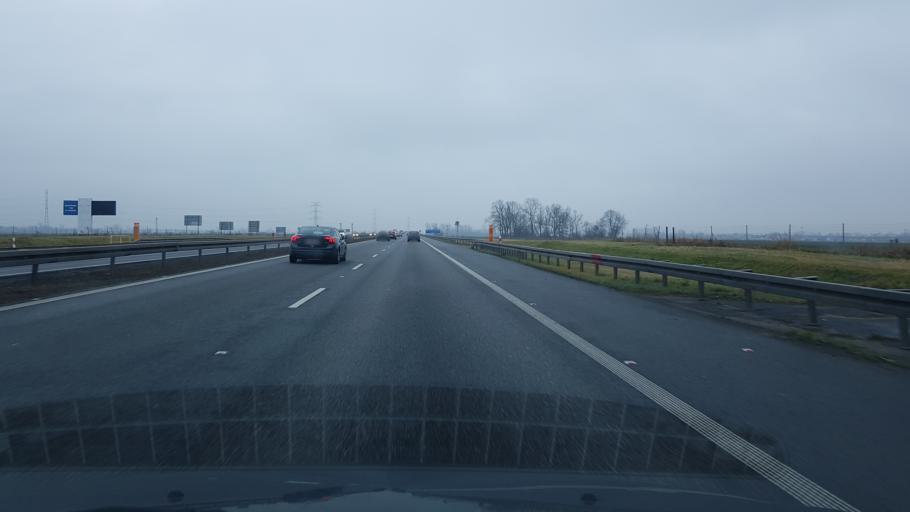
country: PL
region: Lower Silesian Voivodeship
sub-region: Powiat wroclawski
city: Zorawina
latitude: 51.0003
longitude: 17.0397
